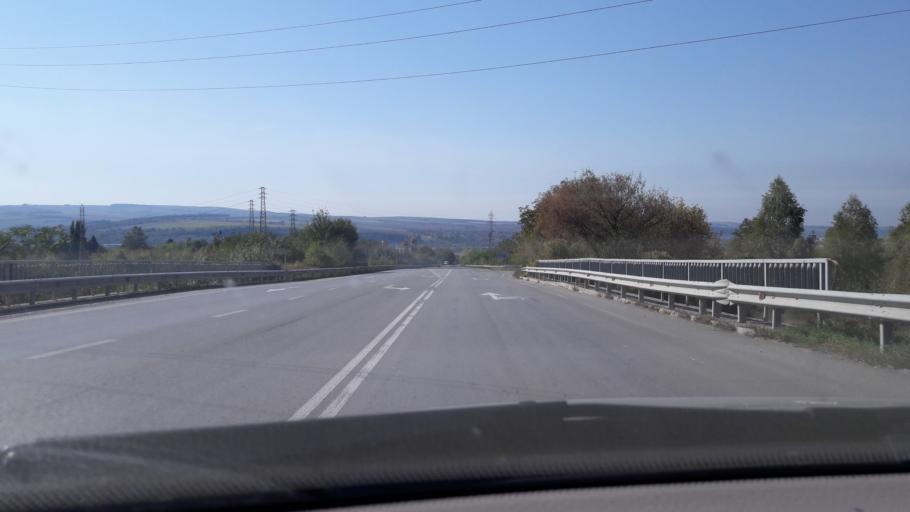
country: BG
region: Razgrad
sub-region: Obshtina Razgrad
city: Razgrad
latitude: 43.5451
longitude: 26.5129
